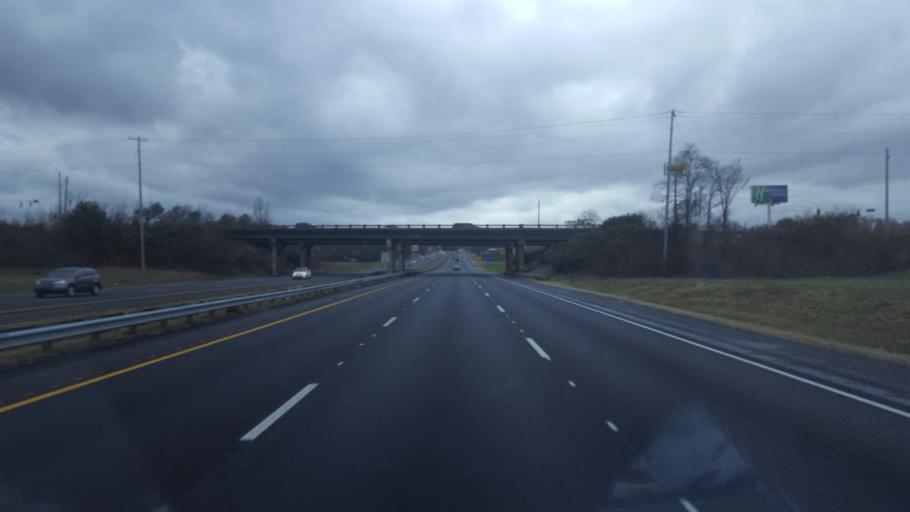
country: US
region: Georgia
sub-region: Catoosa County
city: Ringgold
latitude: 34.9100
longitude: -85.1253
